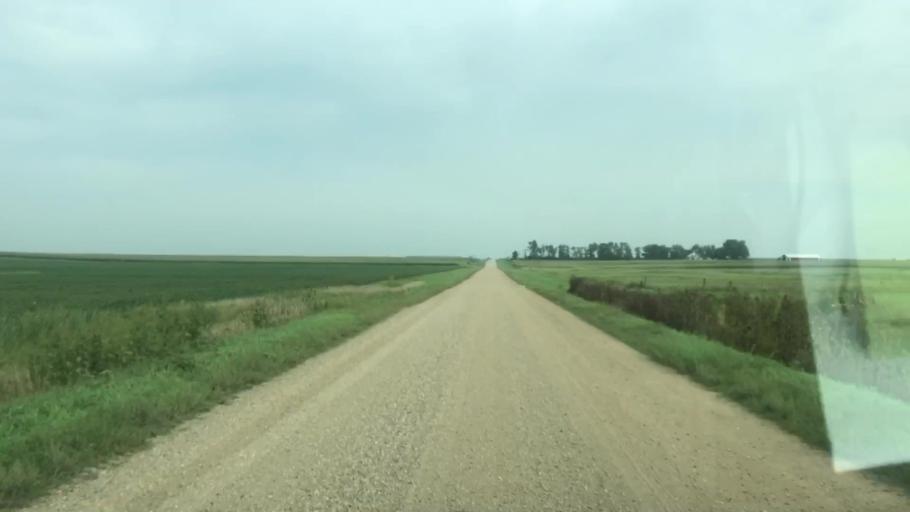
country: US
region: Iowa
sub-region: O'Brien County
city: Sheldon
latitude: 43.2675
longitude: -95.8618
